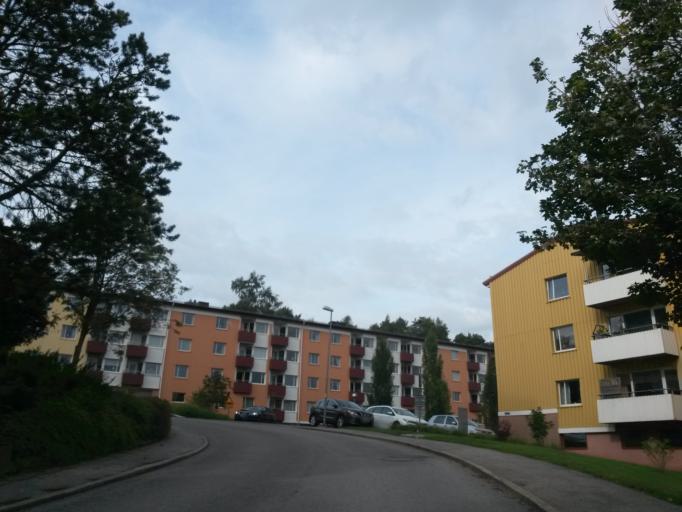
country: SE
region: Vaestra Goetaland
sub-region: Boras Kommun
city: Boras
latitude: 57.7074
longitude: 12.9735
